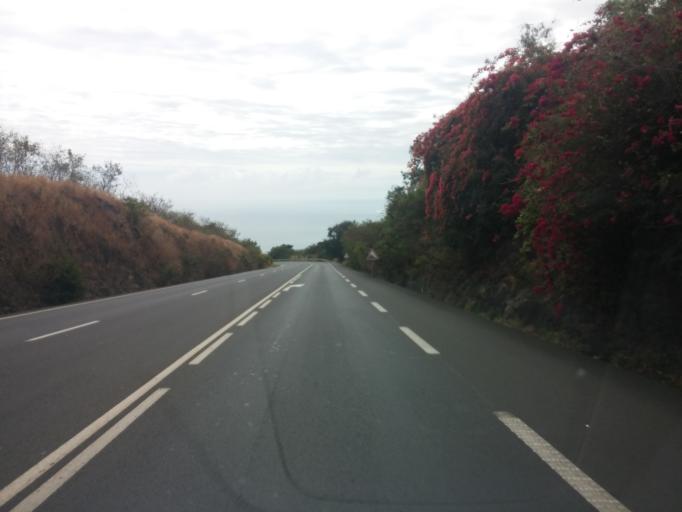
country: RE
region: Reunion
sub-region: Reunion
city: Saint-Paul
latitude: -21.0236
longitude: 55.2739
